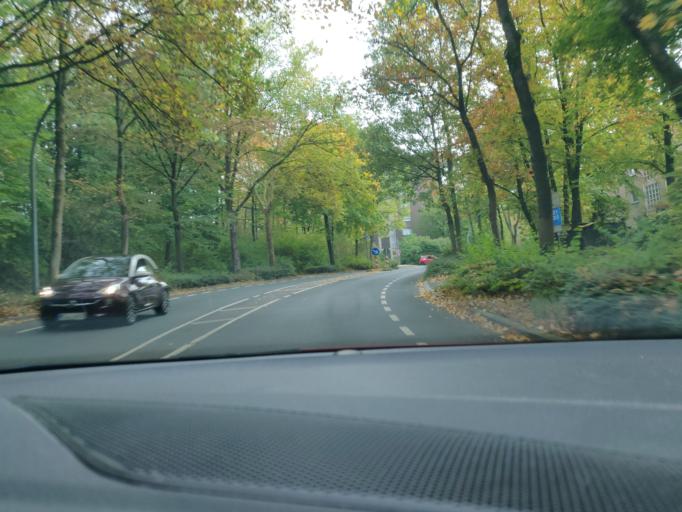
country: DE
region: North Rhine-Westphalia
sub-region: Regierungsbezirk Dusseldorf
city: Velbert
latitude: 51.3411
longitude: 7.0234
